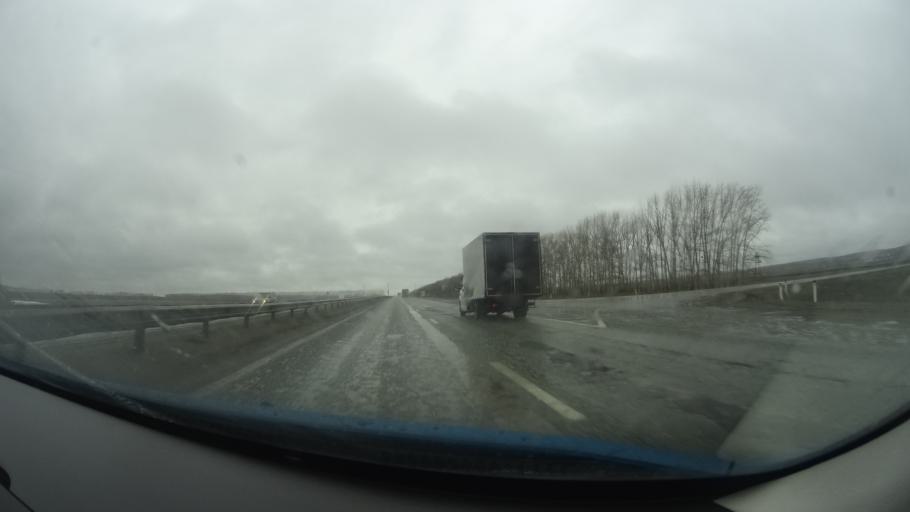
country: RU
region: Bashkortostan
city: Dmitriyevka
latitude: 54.6921
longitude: 55.2900
